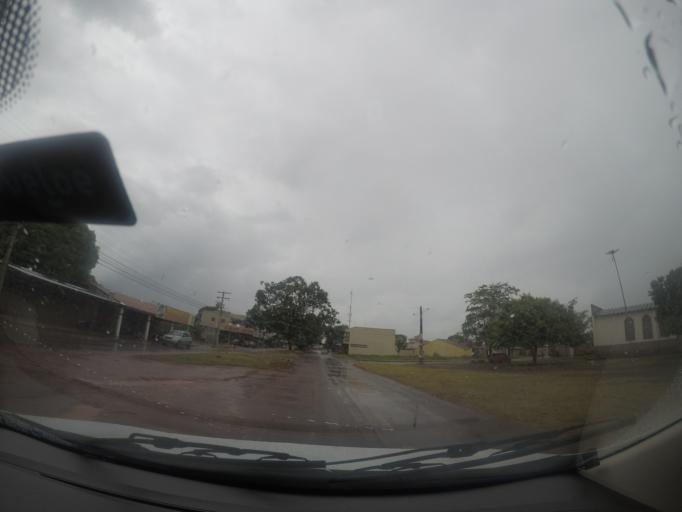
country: BR
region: Goias
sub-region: Trindade
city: Trindade
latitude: -16.6412
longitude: -49.4381
